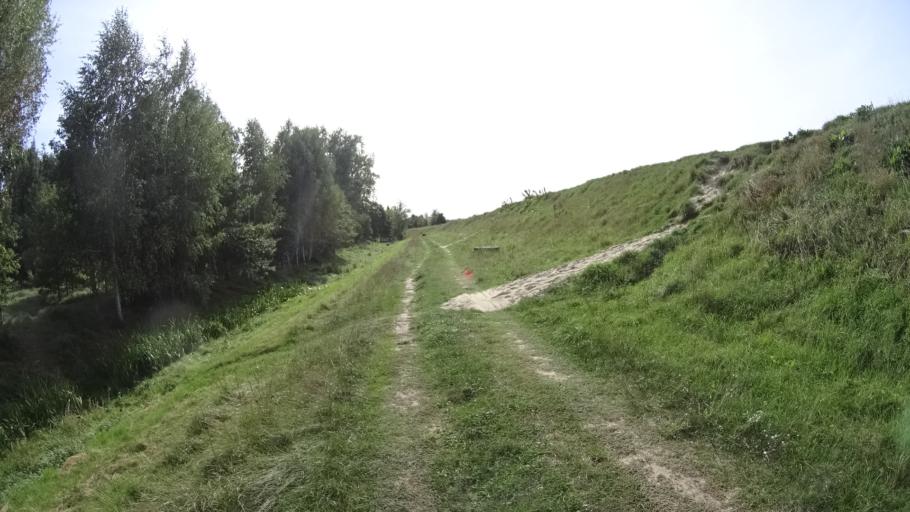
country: PL
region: Masovian Voivodeship
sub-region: Powiat legionowski
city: Serock
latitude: 52.5015
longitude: 21.0840
